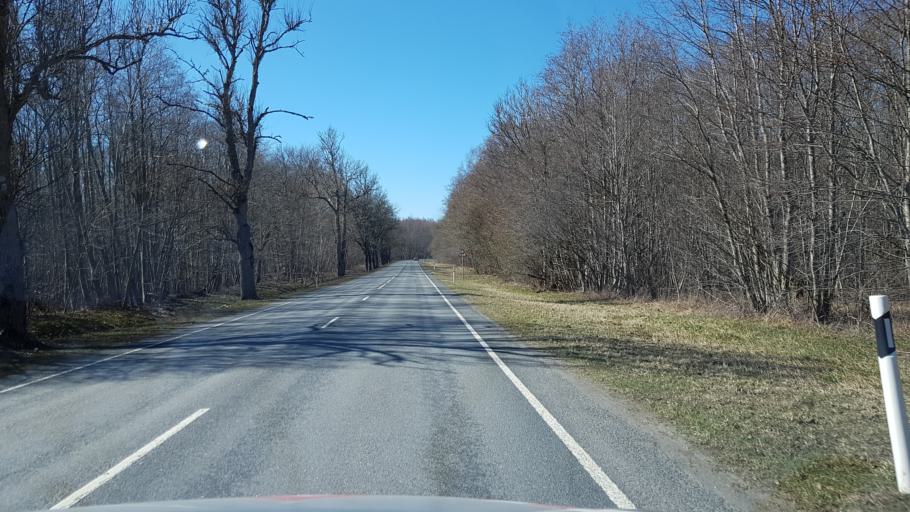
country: EE
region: Laeaene
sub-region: Haapsalu linn
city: Haapsalu
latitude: 58.9178
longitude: 23.4936
